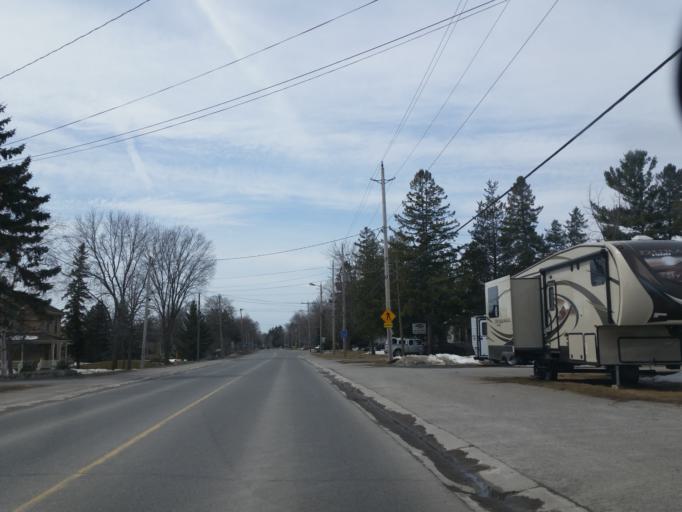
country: CA
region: Ontario
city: Napanee Downtown
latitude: 44.2407
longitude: -76.9630
